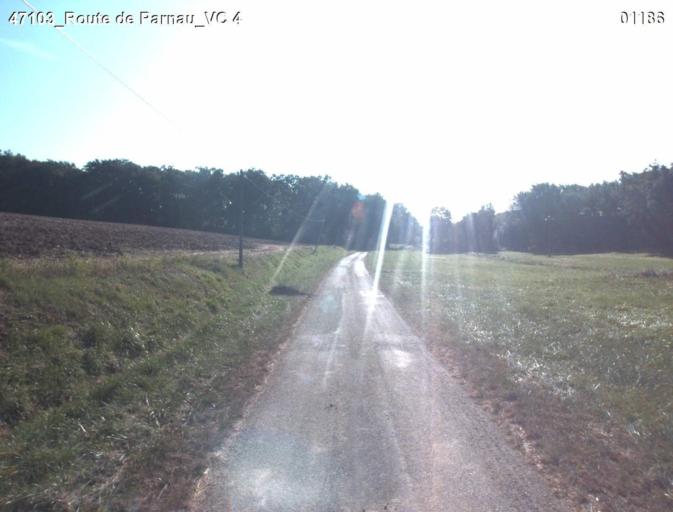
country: FR
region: Aquitaine
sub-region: Departement du Lot-et-Garonne
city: Nerac
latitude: 44.0811
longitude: 0.3429
